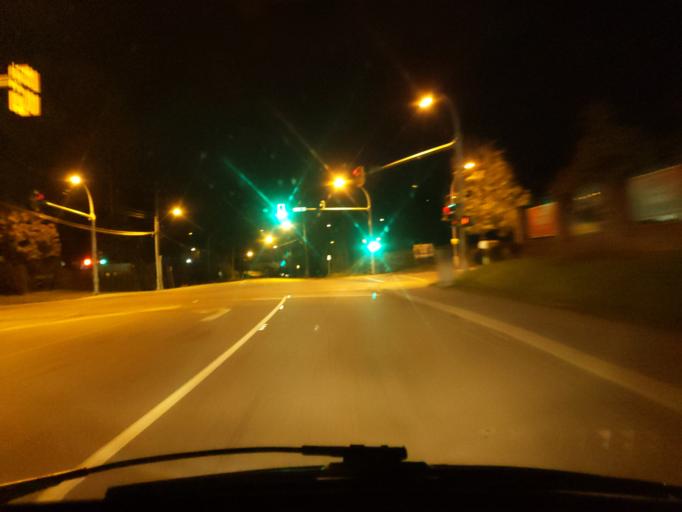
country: CA
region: British Columbia
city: New Westminster
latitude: 49.1976
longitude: -122.8792
